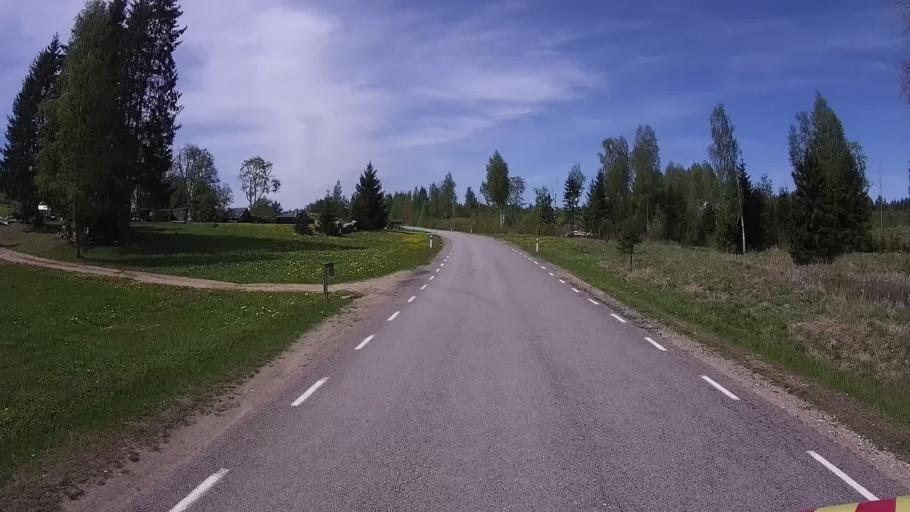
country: EE
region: Vorumaa
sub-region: Antsla vald
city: Vana-Antsla
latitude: 57.6430
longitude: 26.3281
